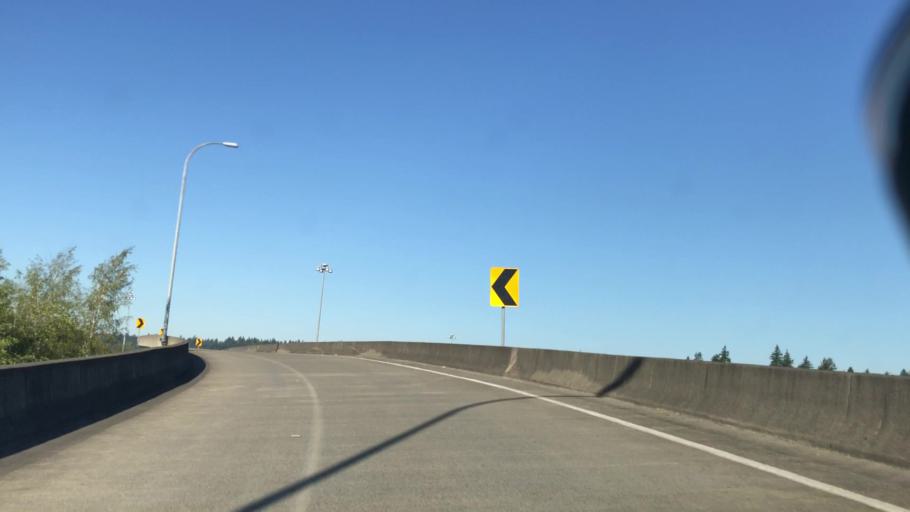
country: US
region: Washington
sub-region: King County
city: Newport
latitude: 47.5806
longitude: -122.1806
